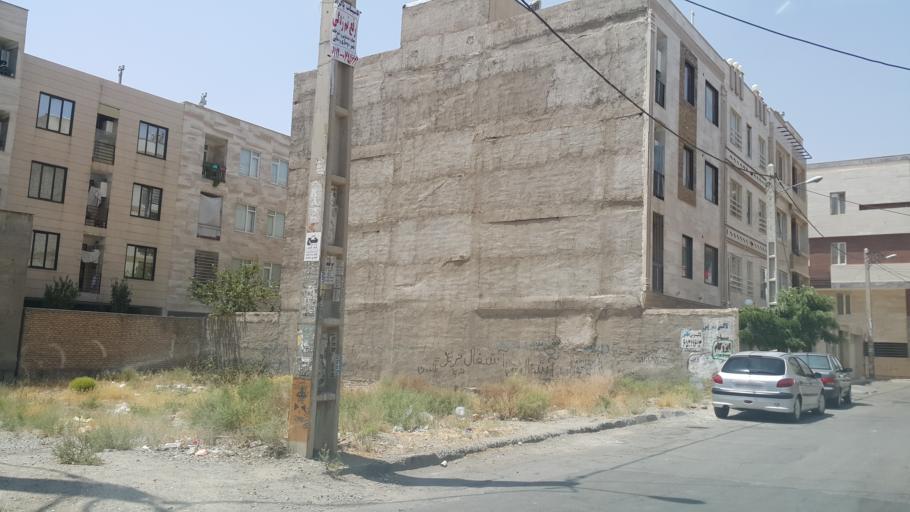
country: IR
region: Tehran
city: Shahre Jadide Andisheh
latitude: 35.6626
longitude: 51.0104
